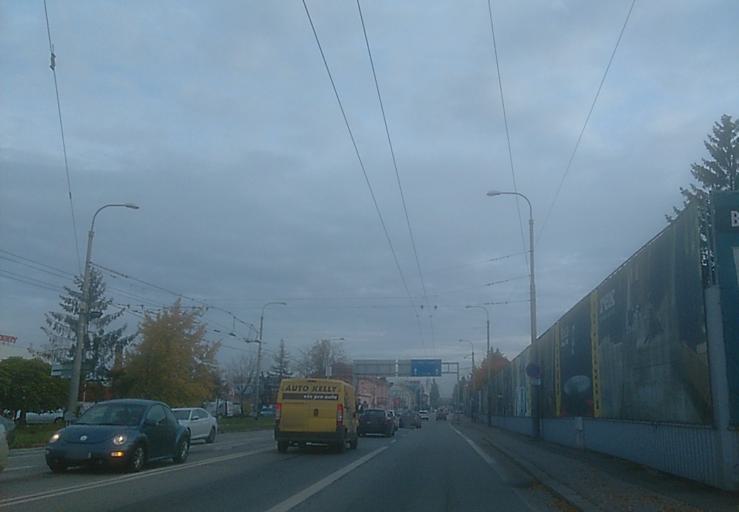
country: CZ
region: Jihocesky
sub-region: Okres Ceske Budejovice
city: Ceske Budejovice
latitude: 48.9896
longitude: 14.4745
